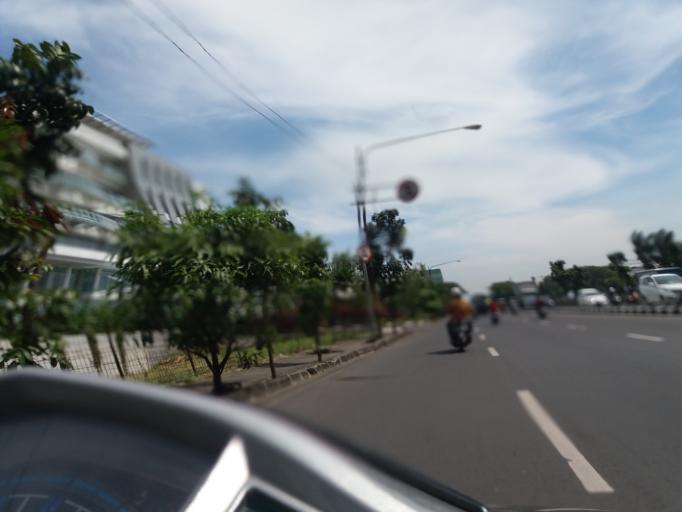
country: ID
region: West Java
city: Bandung
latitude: -6.9490
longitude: 107.6166
